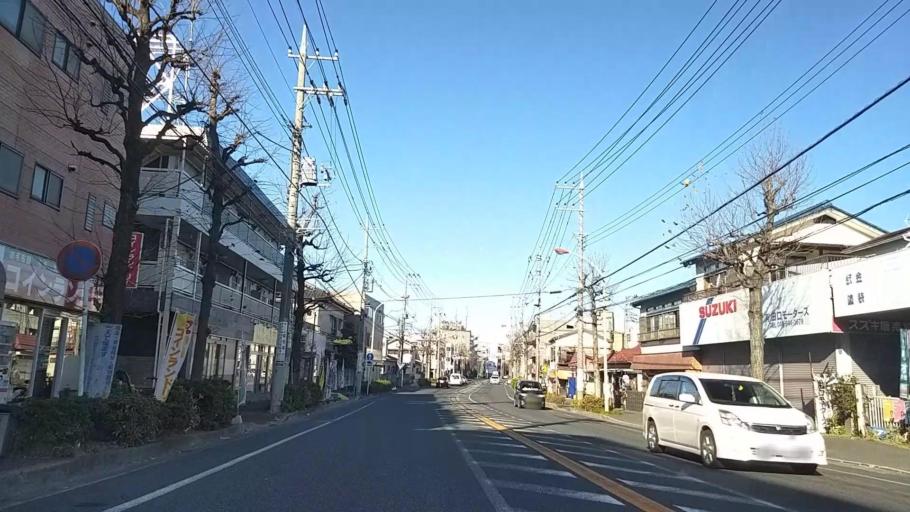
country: JP
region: Tokyo
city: Chofugaoka
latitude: 35.6295
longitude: 139.5381
